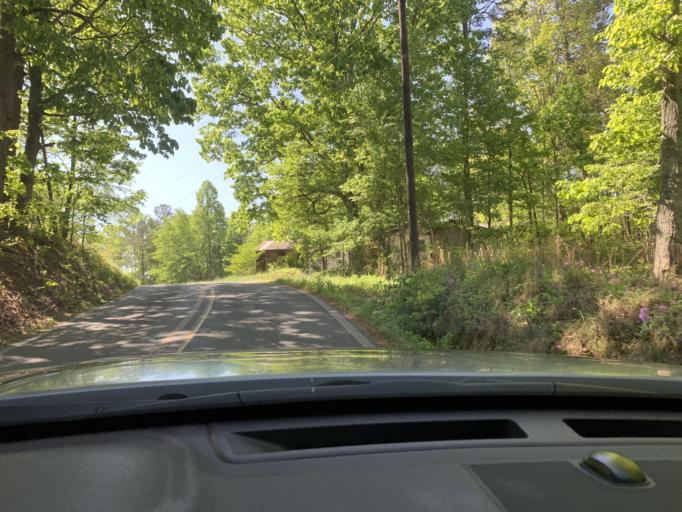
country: US
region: Georgia
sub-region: Haralson County
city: Buchanan
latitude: 33.9096
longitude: -85.2002
